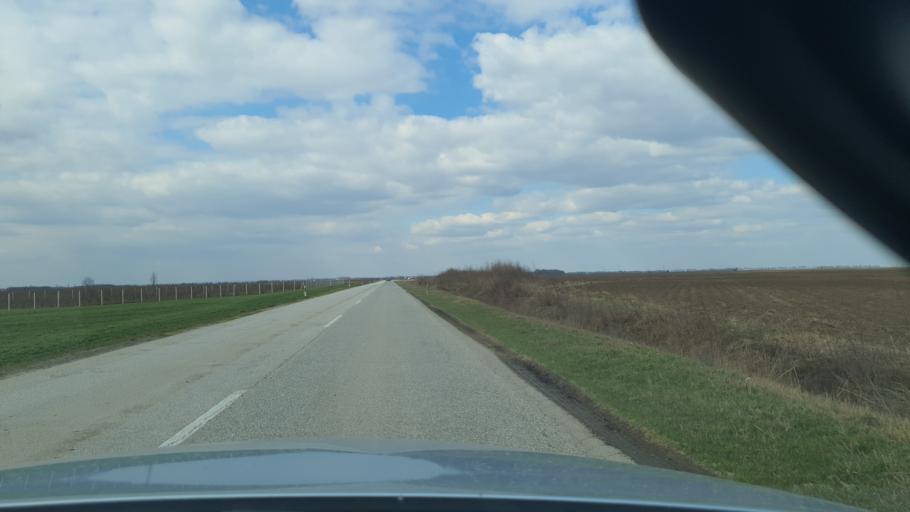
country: RS
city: Obrovac
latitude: 45.4224
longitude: 19.3943
